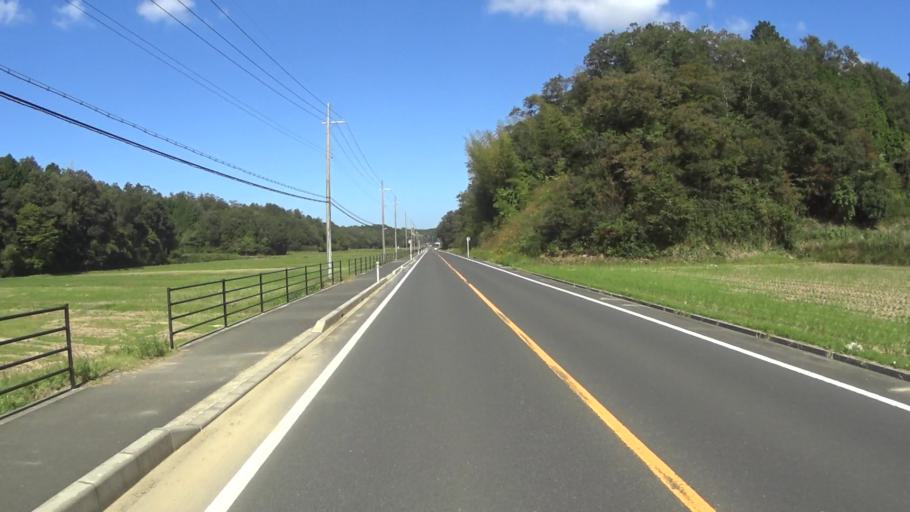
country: JP
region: Kyoto
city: Miyazu
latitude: 35.6450
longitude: 135.0706
